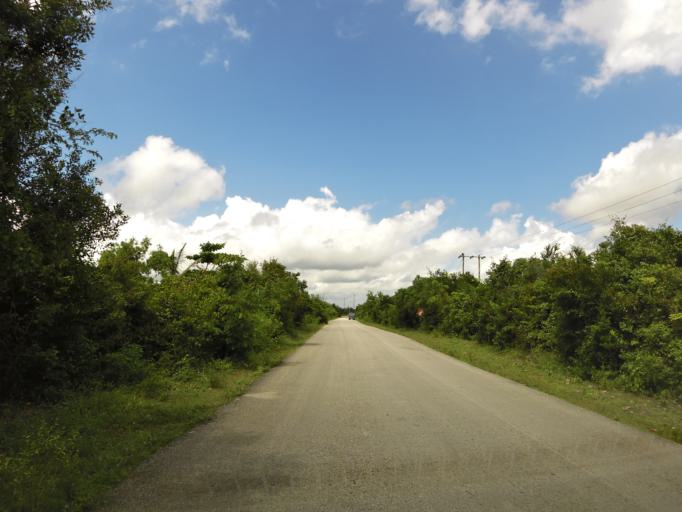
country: TZ
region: Zanzibar Central/South
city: Koani
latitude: -6.1499
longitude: 39.4281
